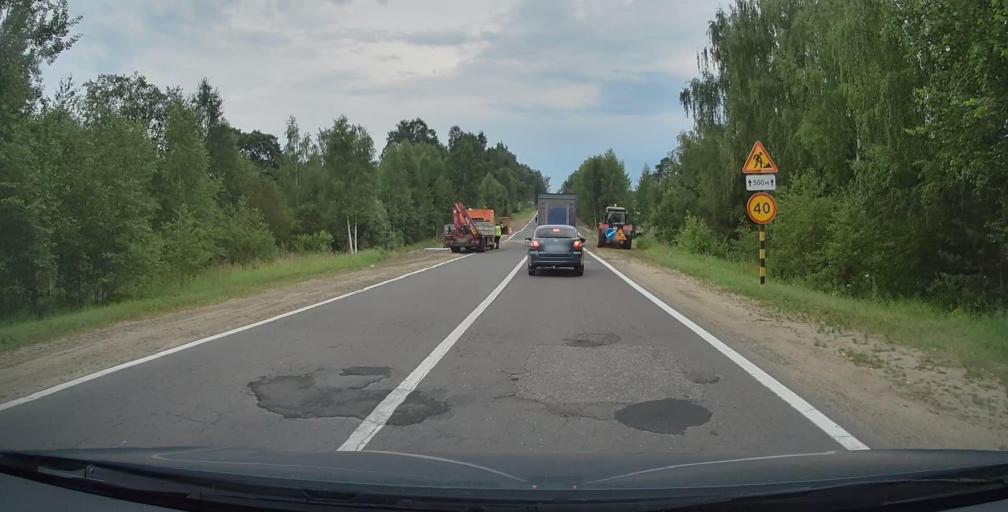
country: RU
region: Jaroslavl
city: Myshkin
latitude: 57.8560
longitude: 38.5096
